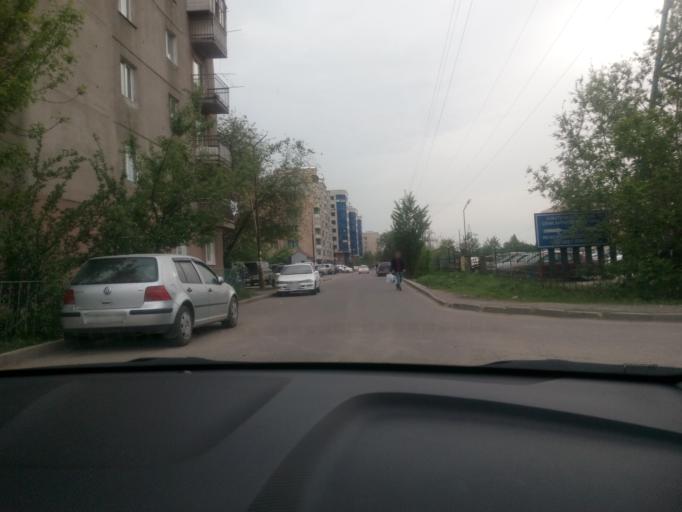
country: KZ
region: Almaty Qalasy
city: Almaty
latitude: 43.2409
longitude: 76.8284
